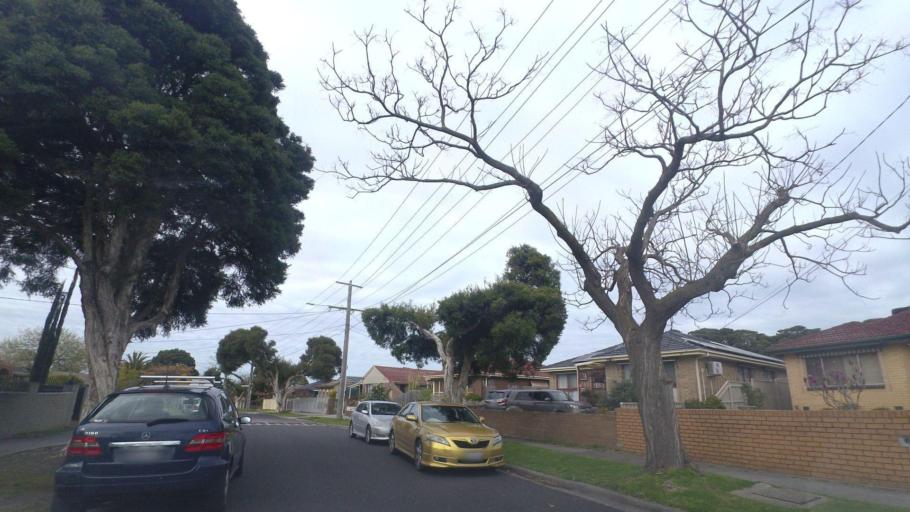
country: AU
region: Victoria
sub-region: Kingston
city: Clayton South
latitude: -37.9442
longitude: 145.1327
